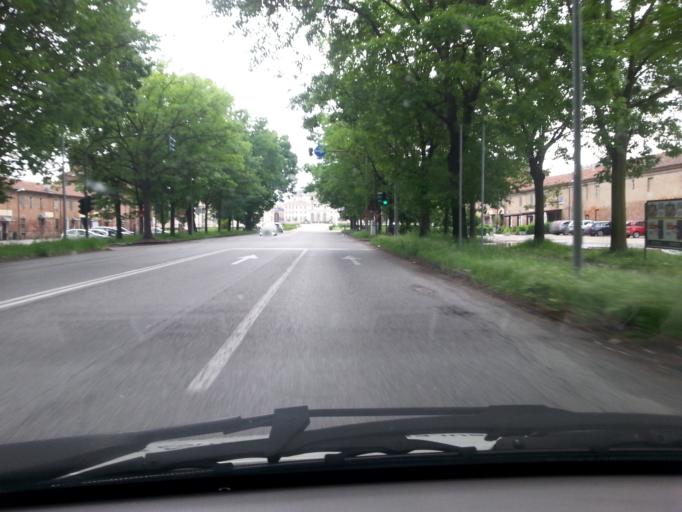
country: IT
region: Piedmont
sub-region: Provincia di Torino
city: Garino
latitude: 44.9983
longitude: 7.6078
